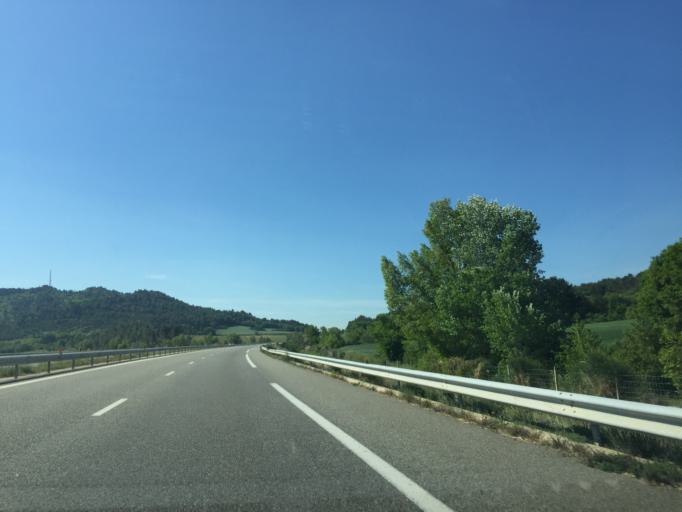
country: FR
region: Provence-Alpes-Cote d'Azur
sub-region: Departement des Alpes-de-Haute-Provence
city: Volonne
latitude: 44.1028
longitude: 5.9944
